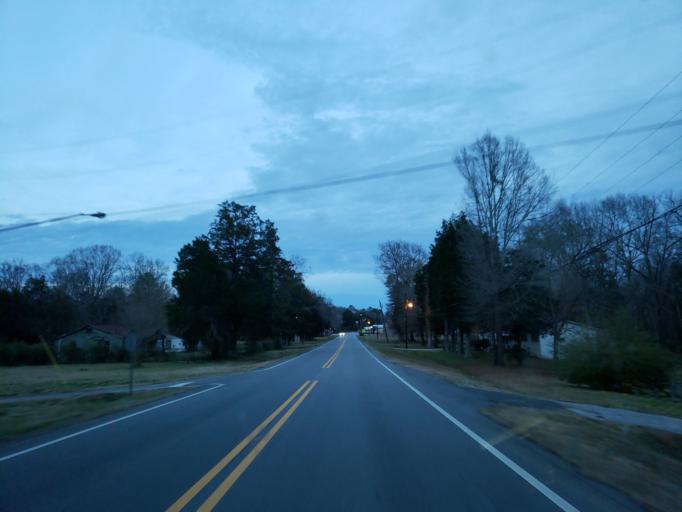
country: US
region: Alabama
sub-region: Sumter County
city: Livingston
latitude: 32.8198
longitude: -88.1621
